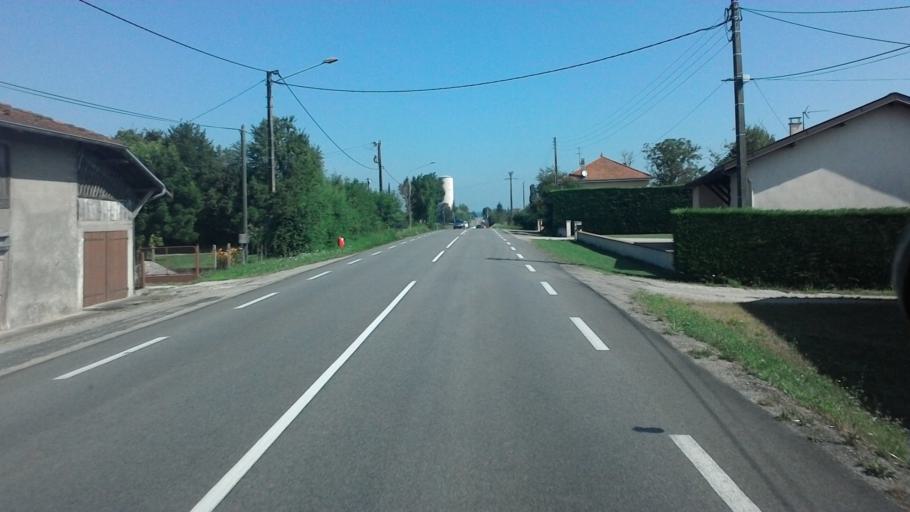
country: FR
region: Rhone-Alpes
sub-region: Departement de l'Ain
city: Montrevel-en-Bresse
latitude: 46.3610
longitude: 5.1226
